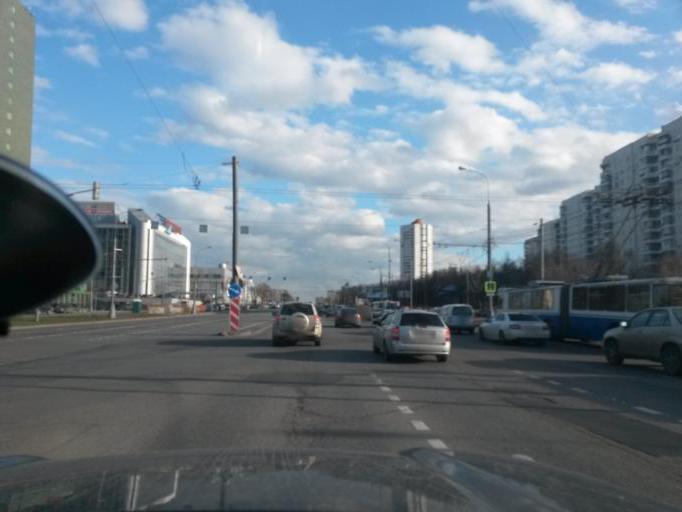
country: RU
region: Moscow
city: Orekhovo-Borisovo
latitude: 55.6196
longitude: 37.7129
